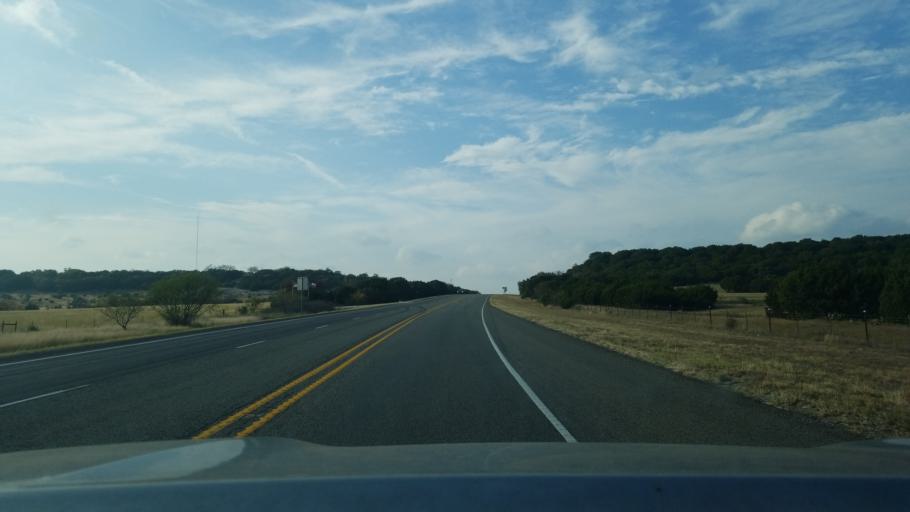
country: US
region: Texas
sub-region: Lampasas County
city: Lampasas
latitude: 31.1385
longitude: -98.3101
